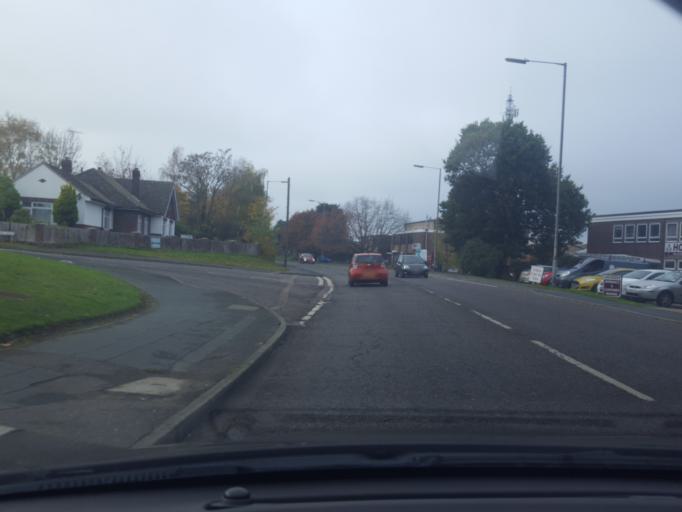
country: GB
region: England
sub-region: Essex
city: Clacton-on-Sea
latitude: 51.8029
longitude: 1.1677
